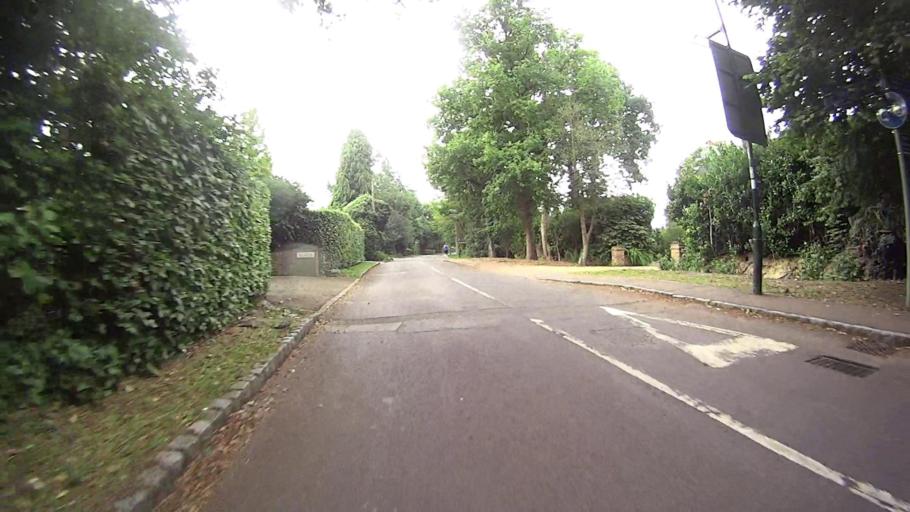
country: GB
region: England
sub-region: West Sussex
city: Maidenbower
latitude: 51.1138
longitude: -0.1429
